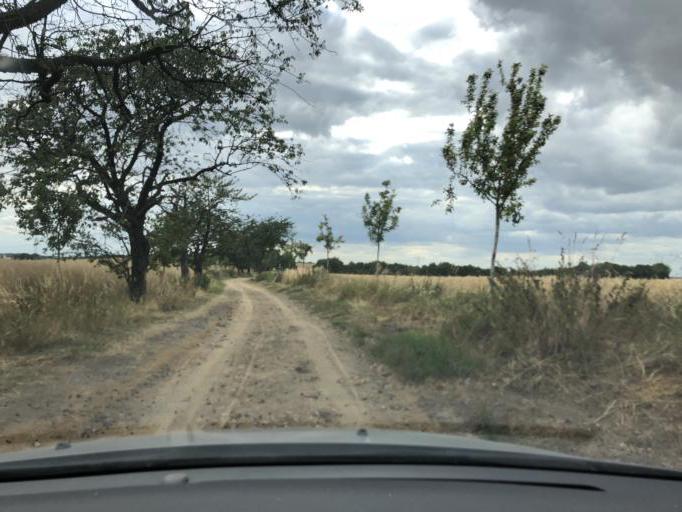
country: DE
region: Saxony
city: Geithain
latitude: 51.0255
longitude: 12.6395
